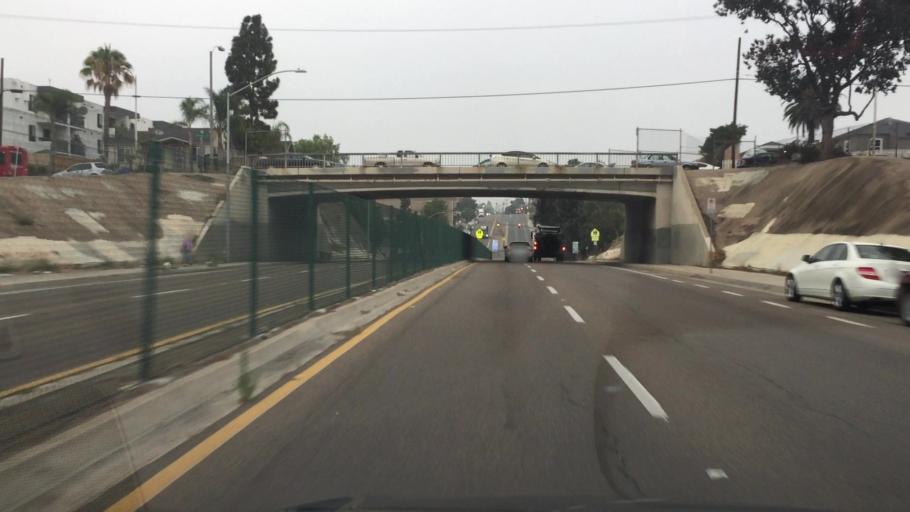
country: US
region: California
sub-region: San Diego County
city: Lemon Grove
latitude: 32.7527
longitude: -117.0794
